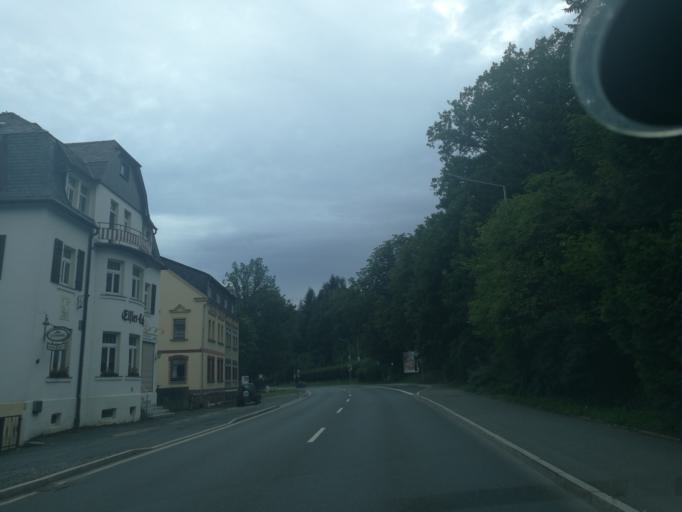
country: DE
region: Saxony
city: Adorf
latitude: 50.3138
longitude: 12.2536
